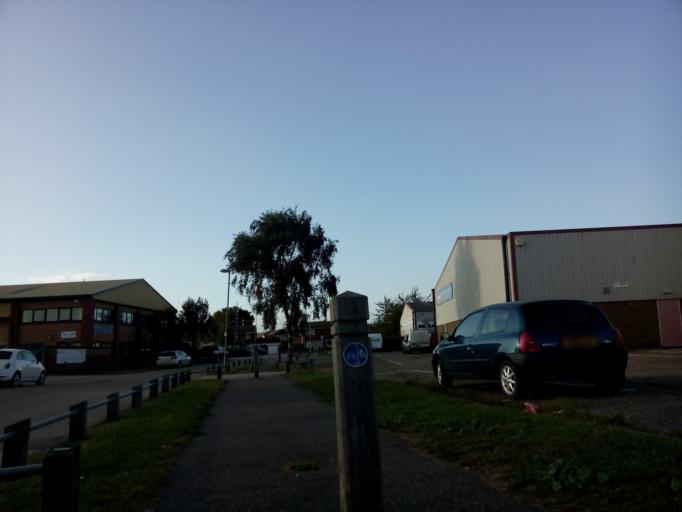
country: GB
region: England
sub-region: Suffolk
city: Bramford
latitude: 52.0653
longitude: 1.1250
